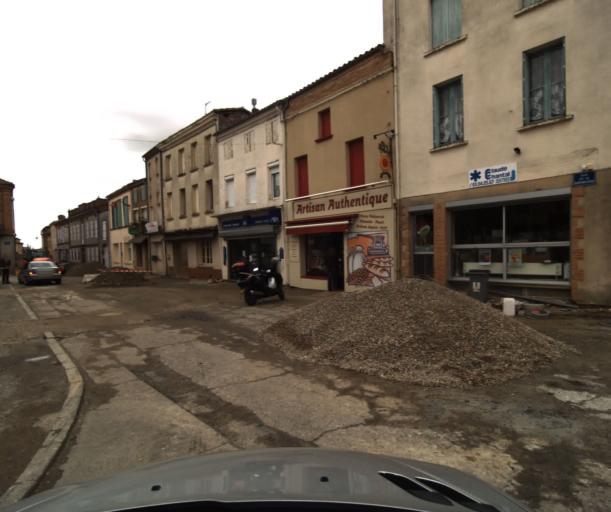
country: FR
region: Midi-Pyrenees
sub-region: Departement du Tarn-et-Garonne
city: Lavit
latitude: 43.9573
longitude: 0.9200
